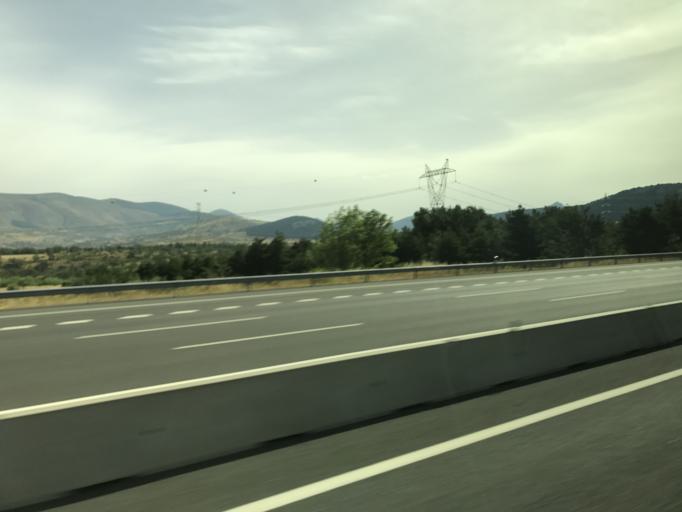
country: ES
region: Castille and Leon
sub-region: Provincia de Segovia
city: Otero de Herreros
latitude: 40.7348
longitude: -4.2042
